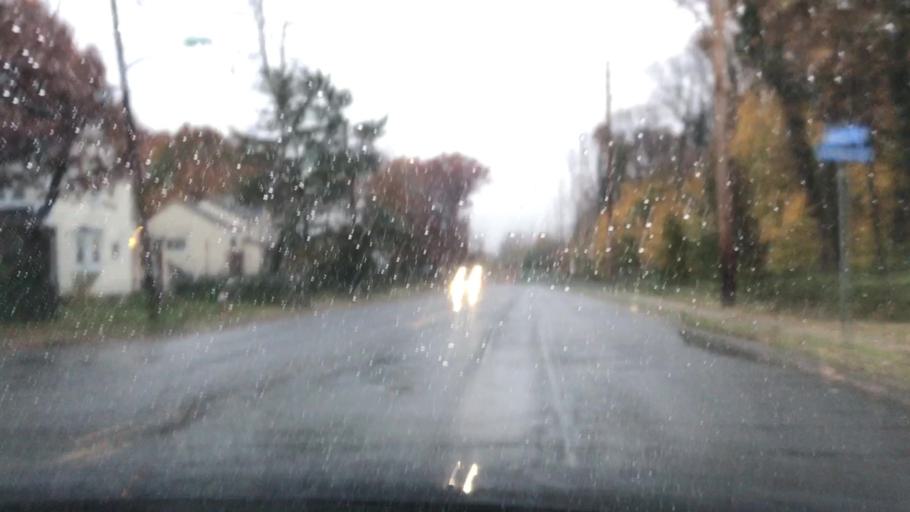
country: US
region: New Jersey
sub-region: Bergen County
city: Teaneck
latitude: 40.9070
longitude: -74.0049
